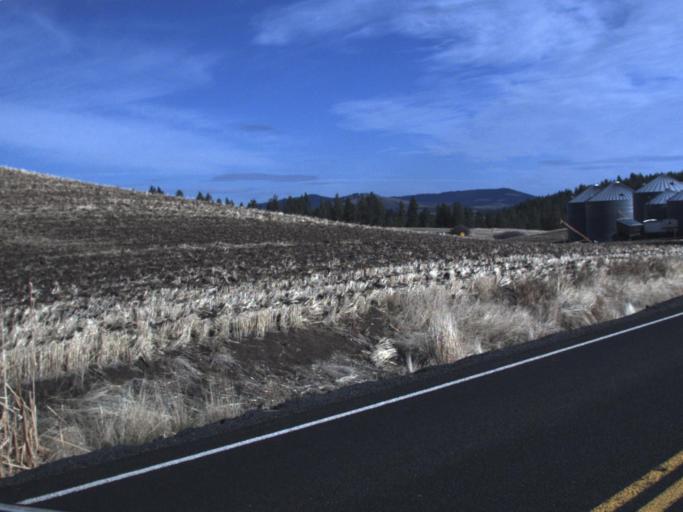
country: US
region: Washington
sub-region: Whitman County
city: Pullman
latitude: 46.9395
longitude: -117.1637
